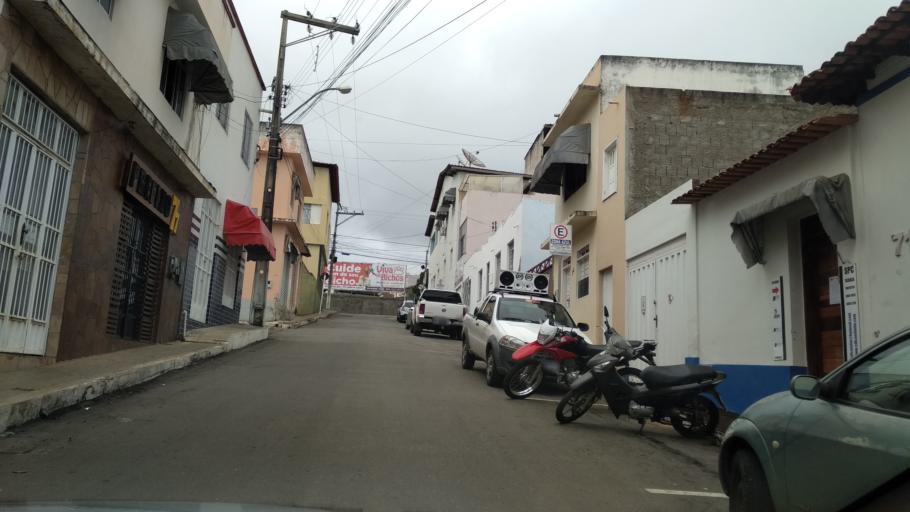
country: BR
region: Bahia
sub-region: Caetite
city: Caetite
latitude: -14.0686
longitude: -42.4875
